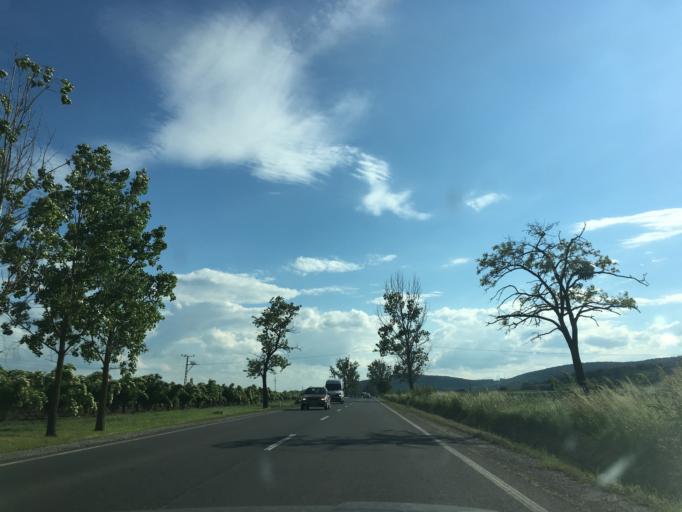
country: HU
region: Borsod-Abauj-Zemplen
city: Sarospatak
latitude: 48.3114
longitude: 21.5299
